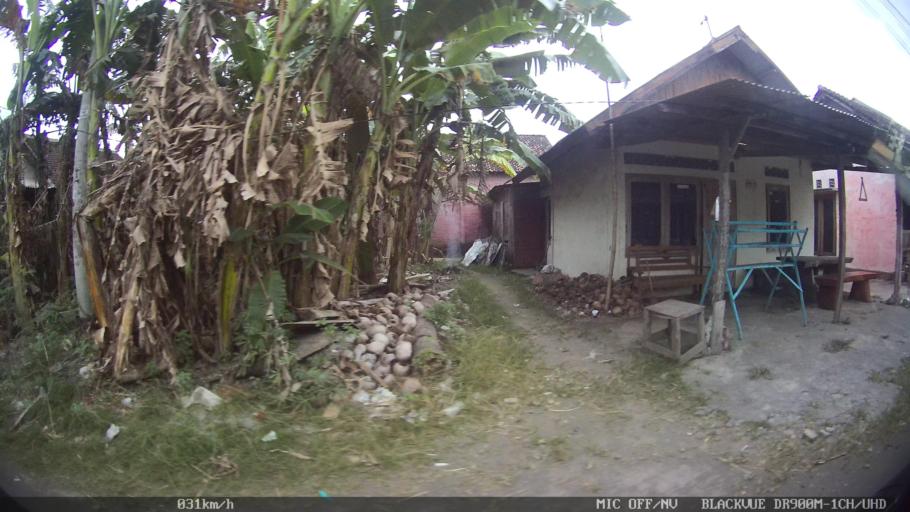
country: ID
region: Daerah Istimewa Yogyakarta
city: Sewon
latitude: -7.8718
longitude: 110.4165
